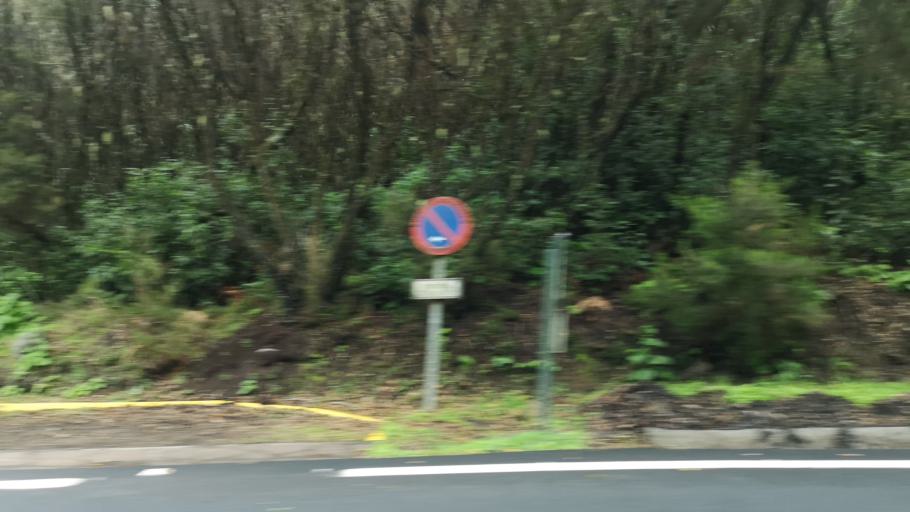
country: ES
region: Canary Islands
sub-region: Provincia de Santa Cruz de Tenerife
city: Vallehermosa
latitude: 28.1269
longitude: -17.2559
